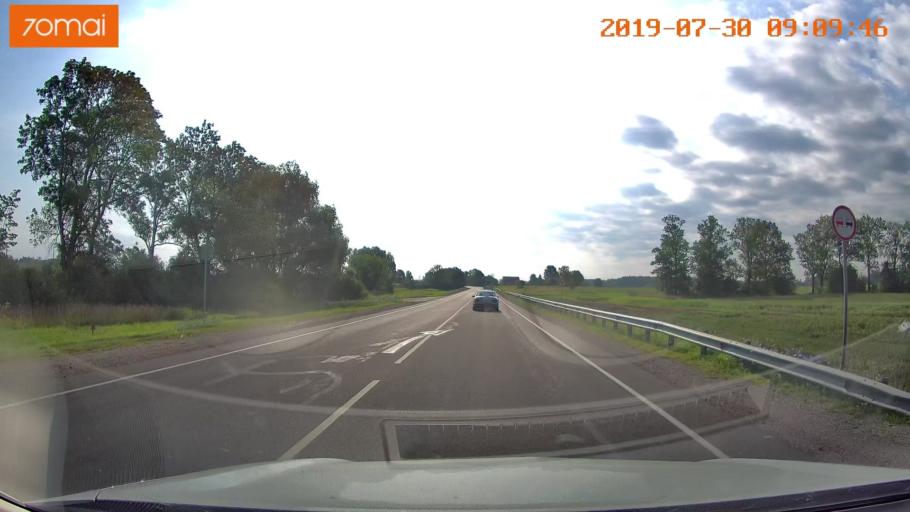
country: RU
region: Kaliningrad
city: Nesterov
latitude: 54.6126
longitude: 22.4148
